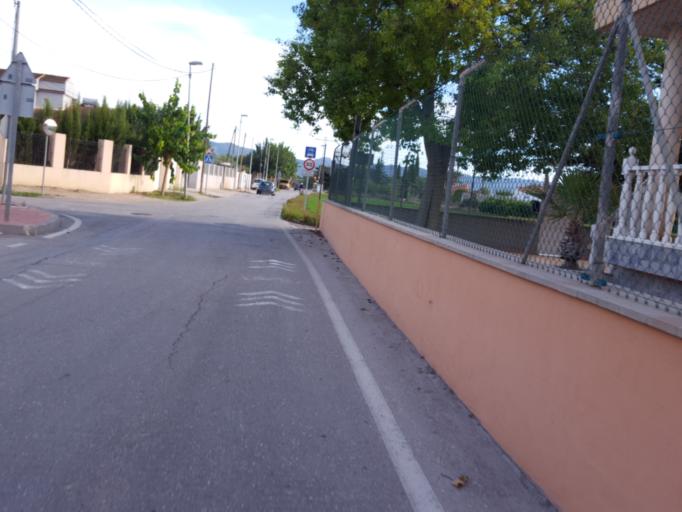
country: ES
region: Murcia
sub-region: Murcia
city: Murcia
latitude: 37.9916
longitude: -1.1737
